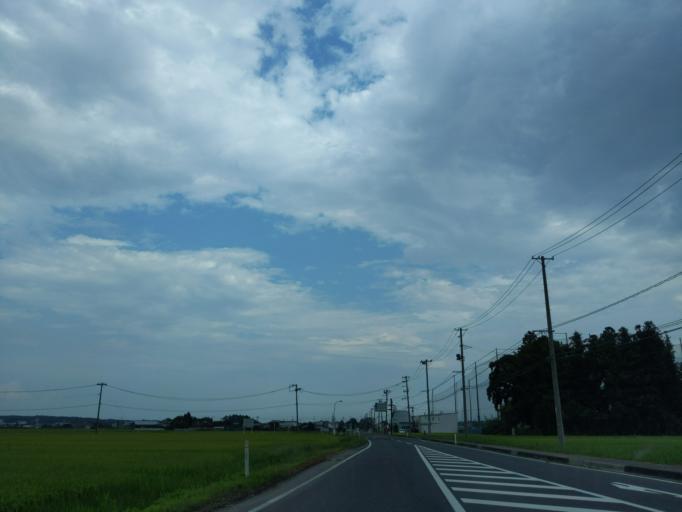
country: JP
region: Miyagi
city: Tomiya
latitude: 38.4333
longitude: 140.8834
